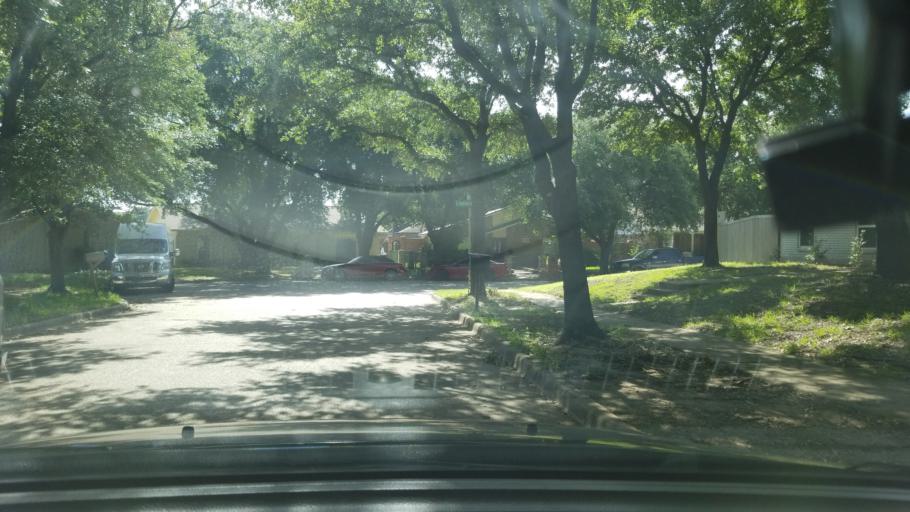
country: US
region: Texas
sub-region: Dallas County
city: Mesquite
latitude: 32.8065
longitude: -96.6919
